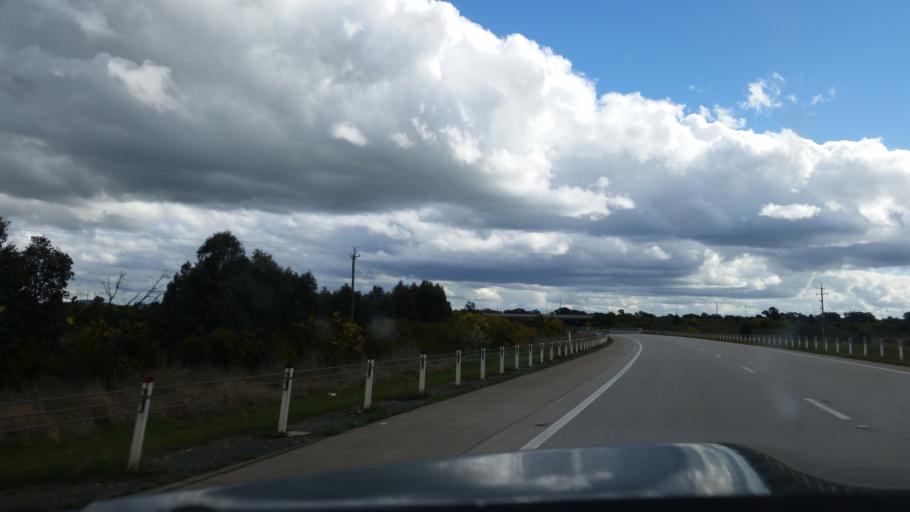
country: AU
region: New South Wales
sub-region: Greater Hume Shire
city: Jindera
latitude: -35.9250
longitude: 147.0124
